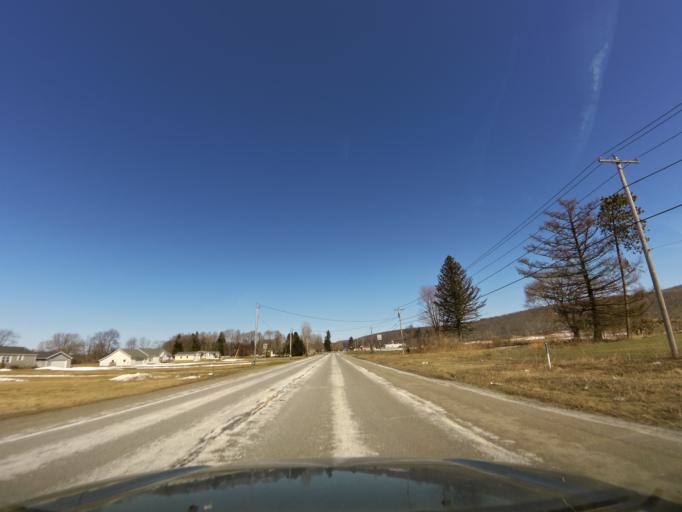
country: US
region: New York
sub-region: Cattaraugus County
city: Franklinville
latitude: 42.3503
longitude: -78.4532
